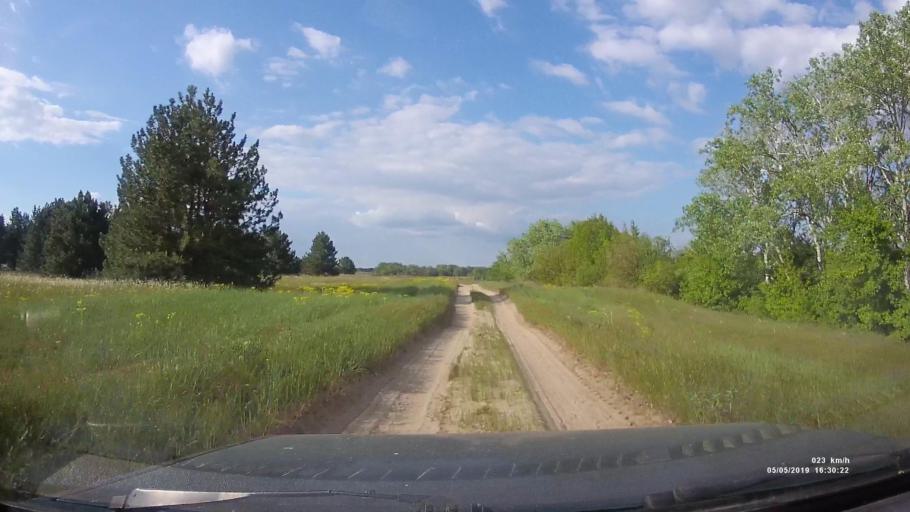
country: RU
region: Rostov
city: Ust'-Donetskiy
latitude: 47.7732
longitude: 41.0157
